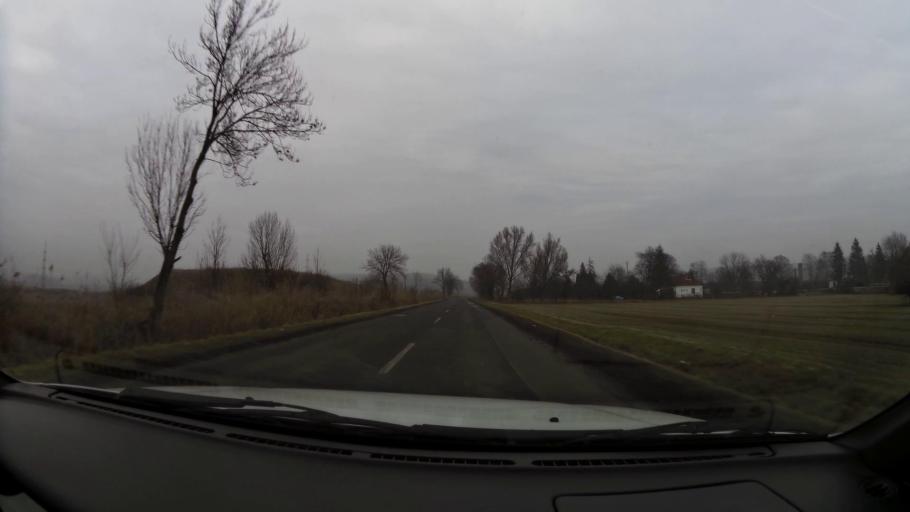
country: HU
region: Borsod-Abauj-Zemplen
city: Izsofalva
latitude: 48.2882
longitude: 20.6587
